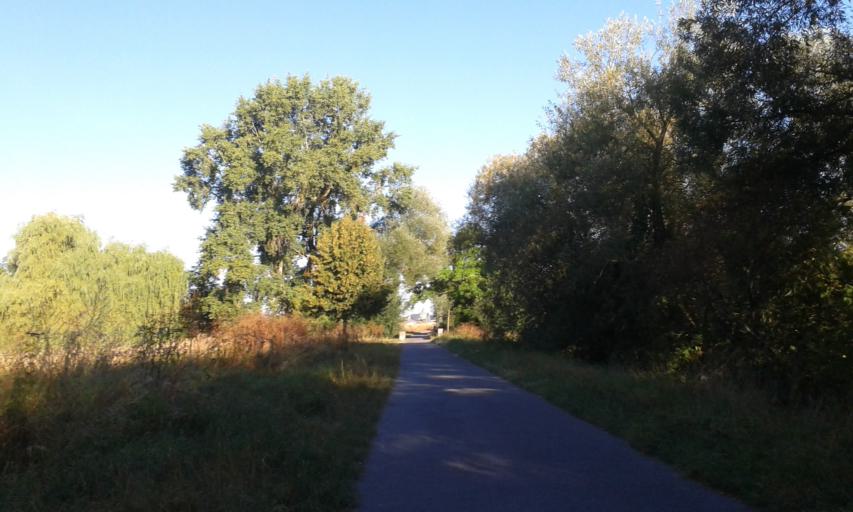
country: DE
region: Bavaria
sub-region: Upper Franconia
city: Bischberg
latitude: 49.9094
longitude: 10.8398
